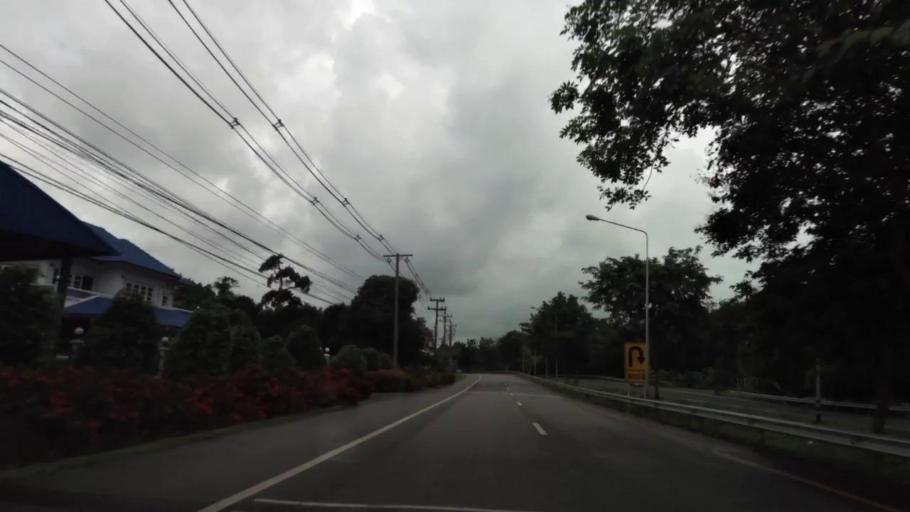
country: TH
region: Chanthaburi
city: Chanthaburi
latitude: 12.5739
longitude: 102.1617
